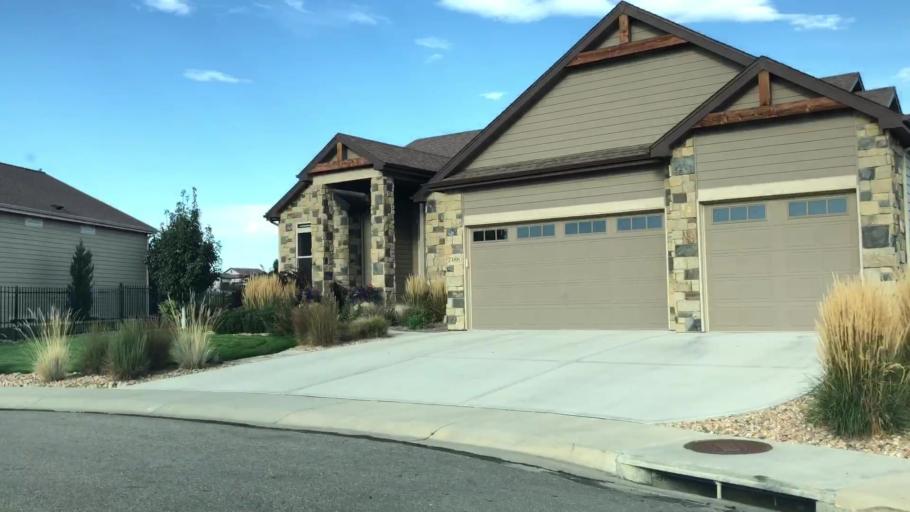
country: US
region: Colorado
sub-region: Weld County
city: Windsor
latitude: 40.4577
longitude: -104.9667
